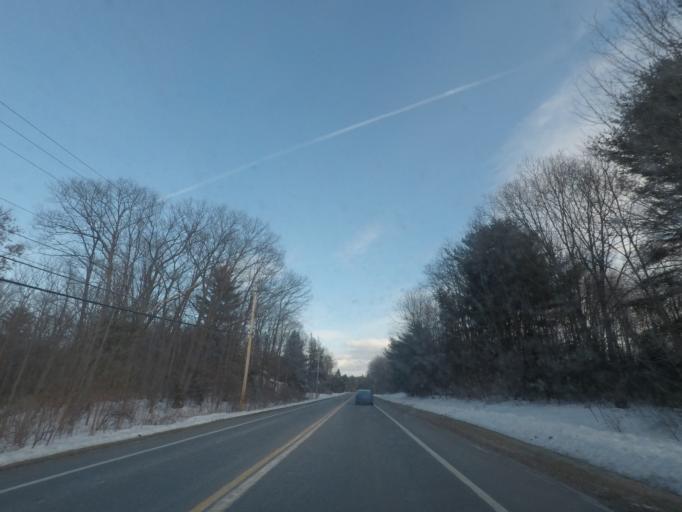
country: US
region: New York
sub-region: Saratoga County
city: Country Knolls
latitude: 42.8402
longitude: -73.8008
